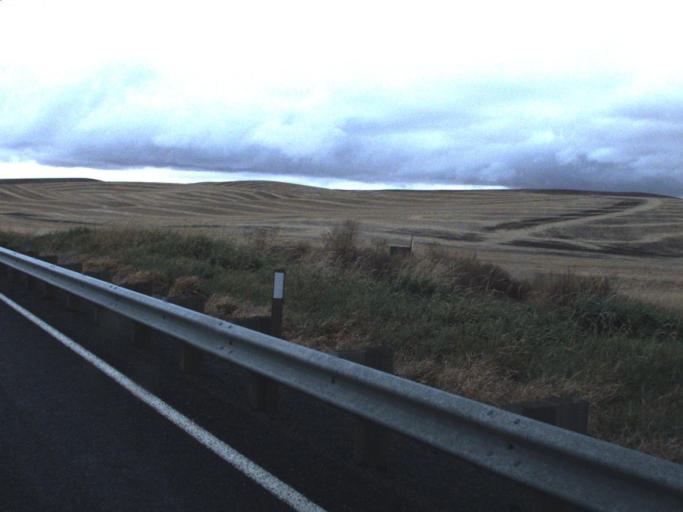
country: US
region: Washington
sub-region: Whitman County
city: Colfax
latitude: 47.1626
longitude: -117.2701
